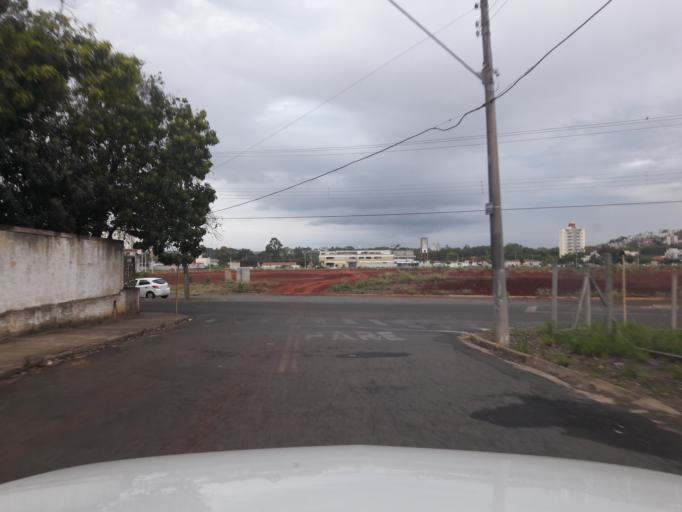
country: BR
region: Sao Paulo
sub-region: Moji-Guacu
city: Mogi-Gaucu
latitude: -22.3687
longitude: -46.9502
